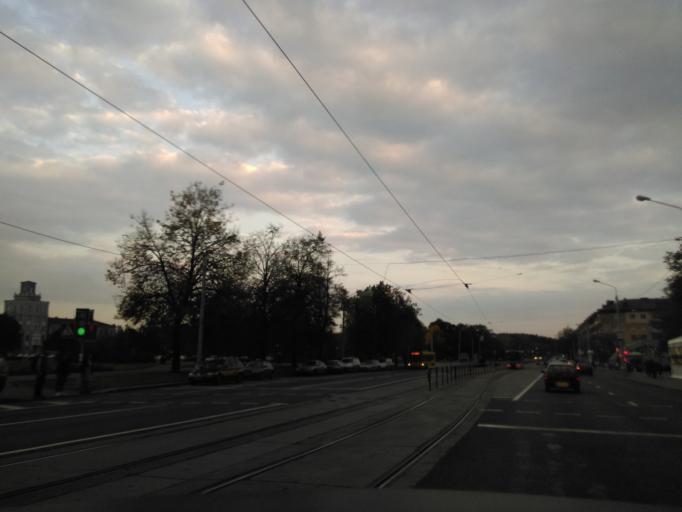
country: BY
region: Minsk
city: Minsk
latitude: 53.8904
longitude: 27.6140
